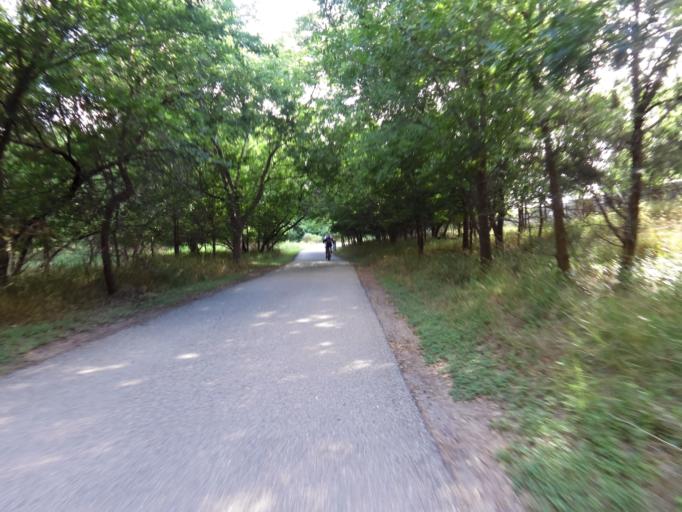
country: US
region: Texas
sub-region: Bexar County
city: Leon Valley
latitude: 29.5529
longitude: -98.6297
